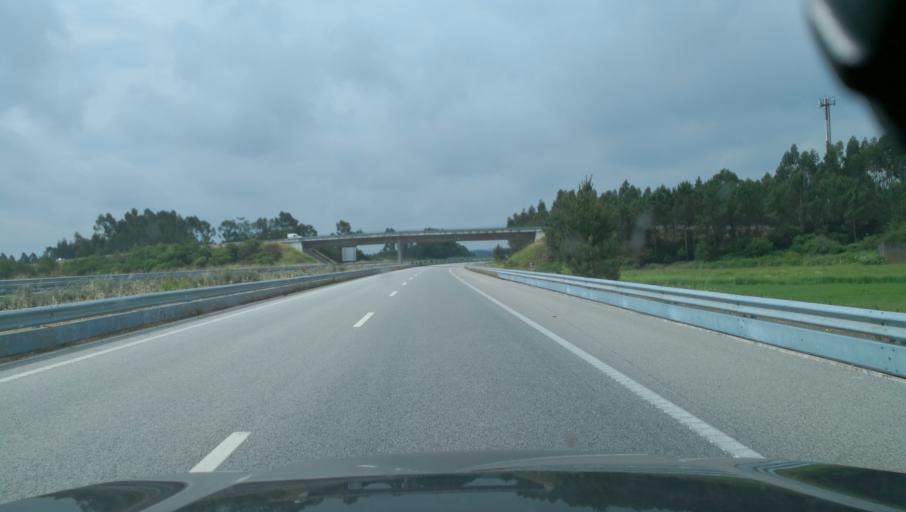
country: PT
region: Coimbra
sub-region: Figueira da Foz
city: Alhadas
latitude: 40.2594
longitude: -8.7619
